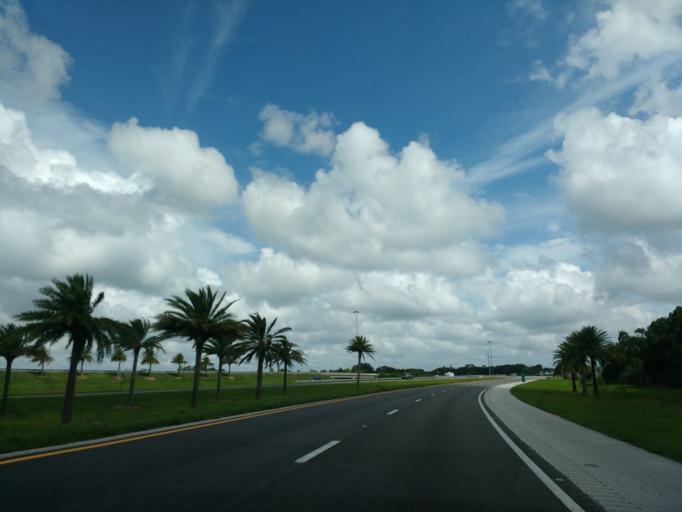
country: US
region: Florida
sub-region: Manatee County
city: Ellenton
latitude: 27.5820
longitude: -82.5155
